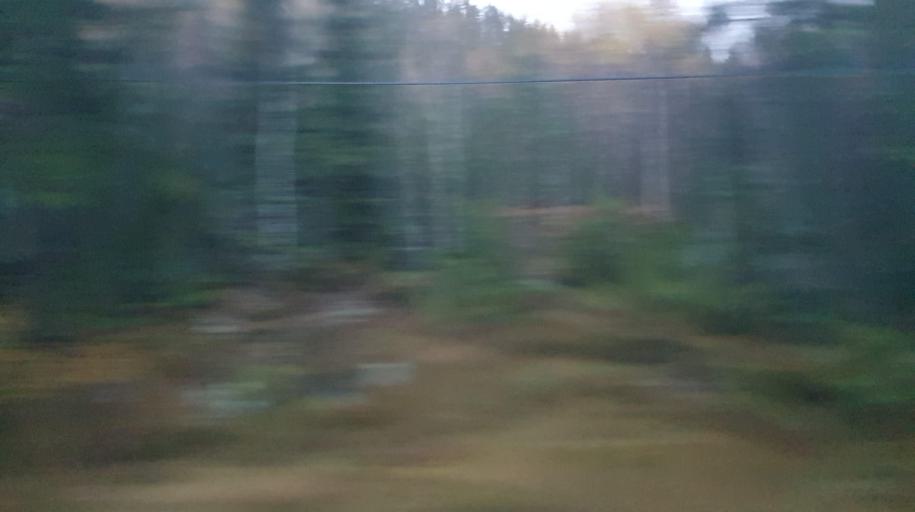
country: NO
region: Buskerud
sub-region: Krodsherad
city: Noresund
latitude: 60.1486
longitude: 9.7616
